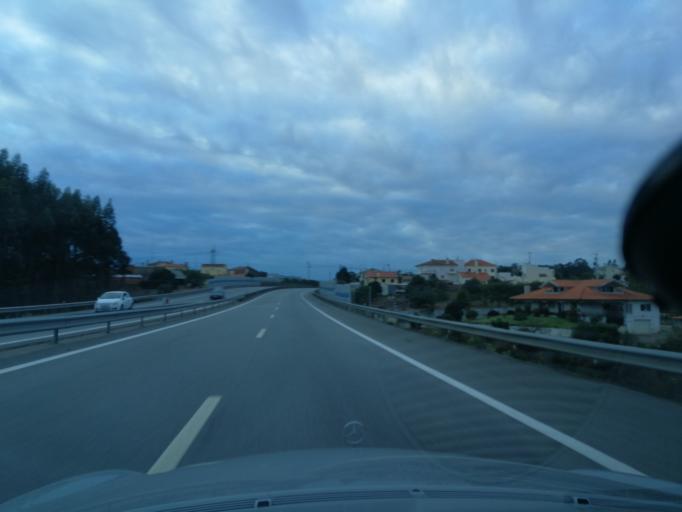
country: PT
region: Aveiro
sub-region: Albergaria-A-Velha
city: Albergaria-a-Velha
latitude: 40.6870
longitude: -8.5102
